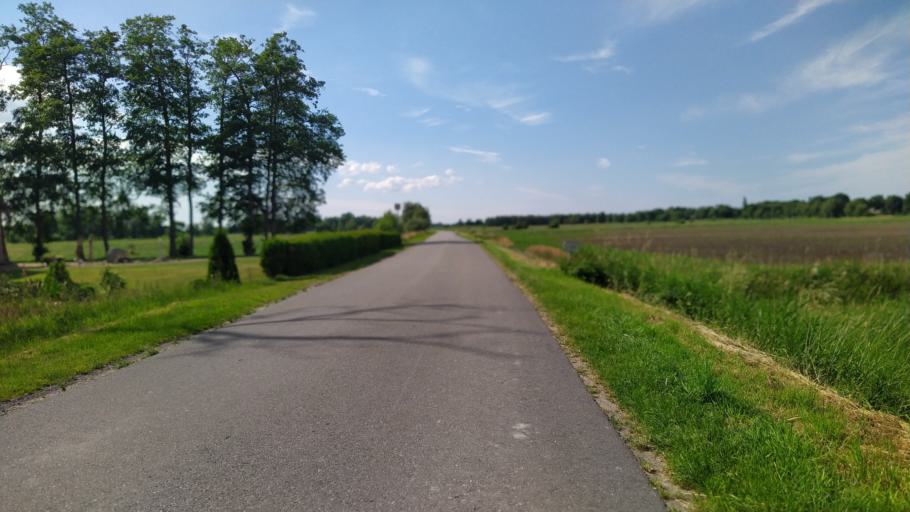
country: DE
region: Lower Saxony
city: Odisheim
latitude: 53.6651
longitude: 8.9285
